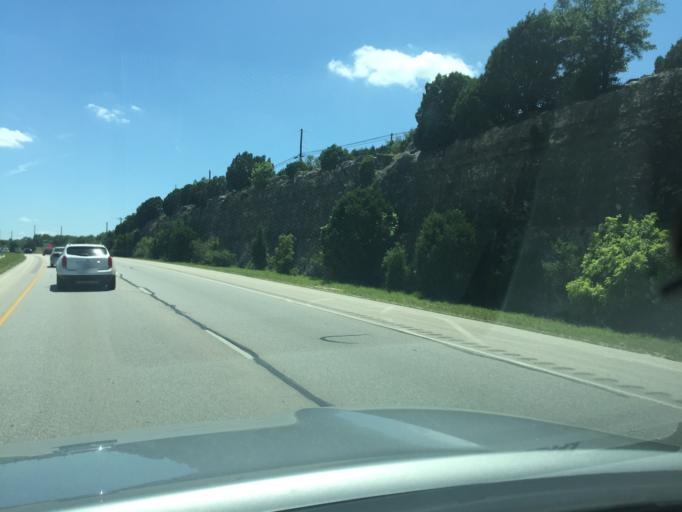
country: US
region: Texas
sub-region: Comal County
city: Bulverde
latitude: 29.7778
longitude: -98.4259
